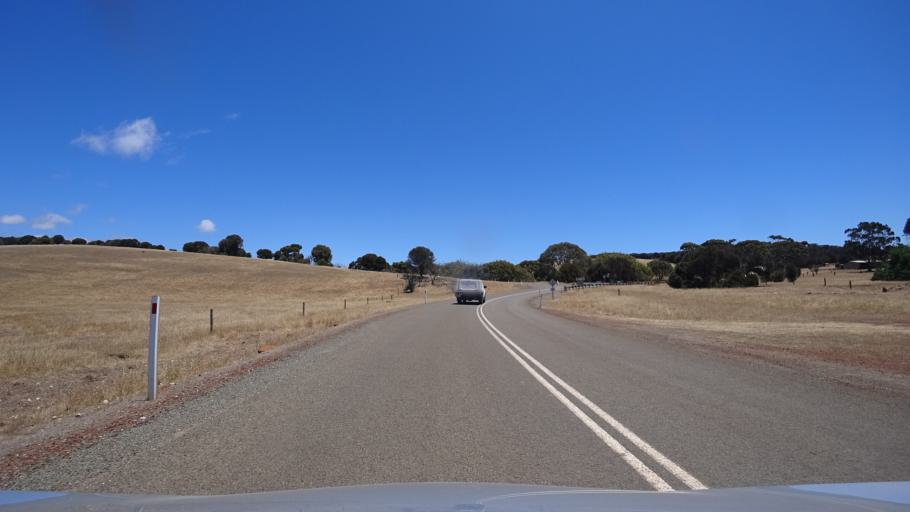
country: AU
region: South Australia
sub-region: Kangaroo Island
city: Kingscote
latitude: -35.6294
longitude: 137.2046
